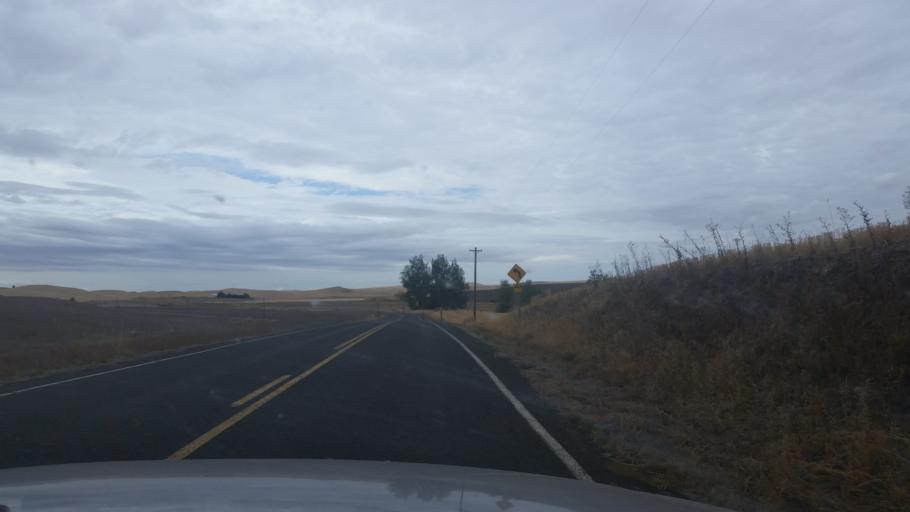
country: US
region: Washington
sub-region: Spokane County
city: Medical Lake
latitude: 47.5217
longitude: -117.8750
